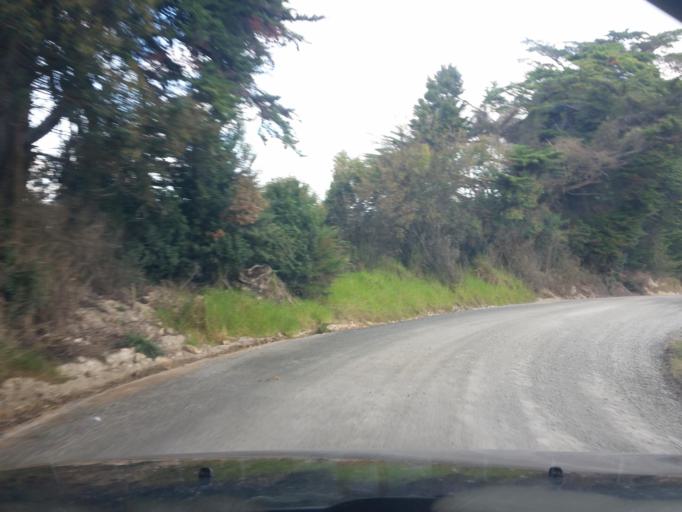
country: NZ
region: Northland
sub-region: Kaipara District
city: Dargaville
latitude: -35.9966
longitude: 173.9505
